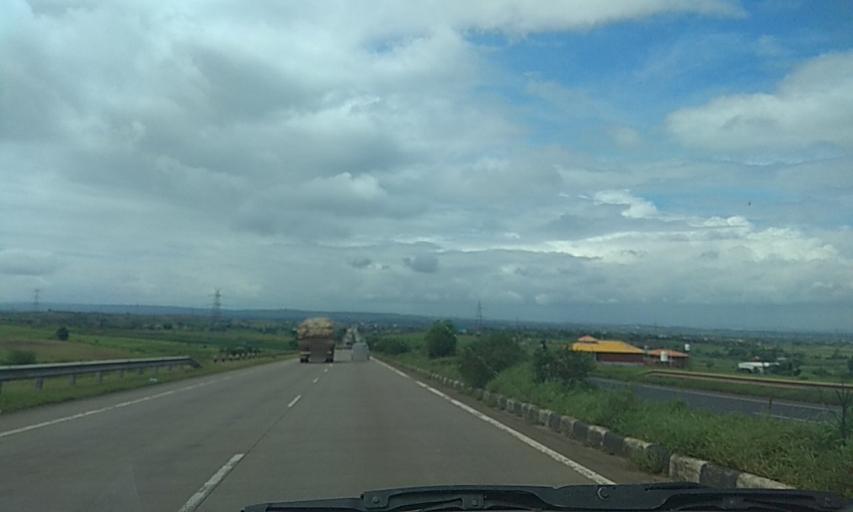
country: IN
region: Maharashtra
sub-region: Kolhapur
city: Kagal
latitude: 16.5008
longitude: 74.3340
